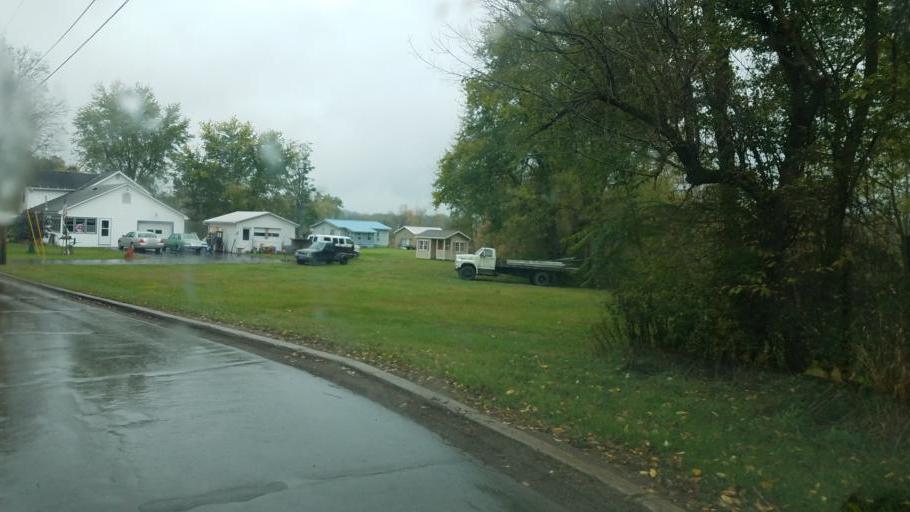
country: US
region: Ohio
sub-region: Holmes County
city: Millersburg
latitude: 40.6298
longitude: -81.9278
